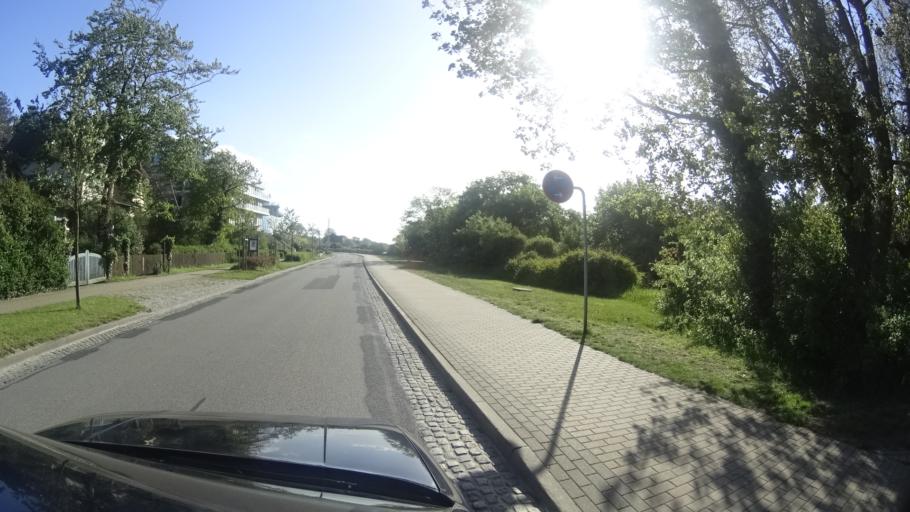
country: DE
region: Mecklenburg-Vorpommern
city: Born
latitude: 54.3851
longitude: 12.4270
